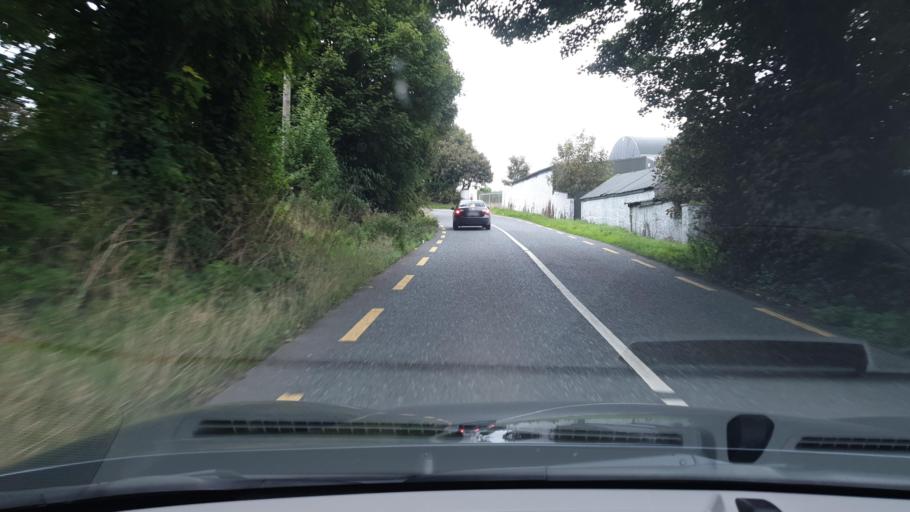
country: IE
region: Leinster
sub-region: Kildare
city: Clane
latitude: 53.2726
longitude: -6.6881
